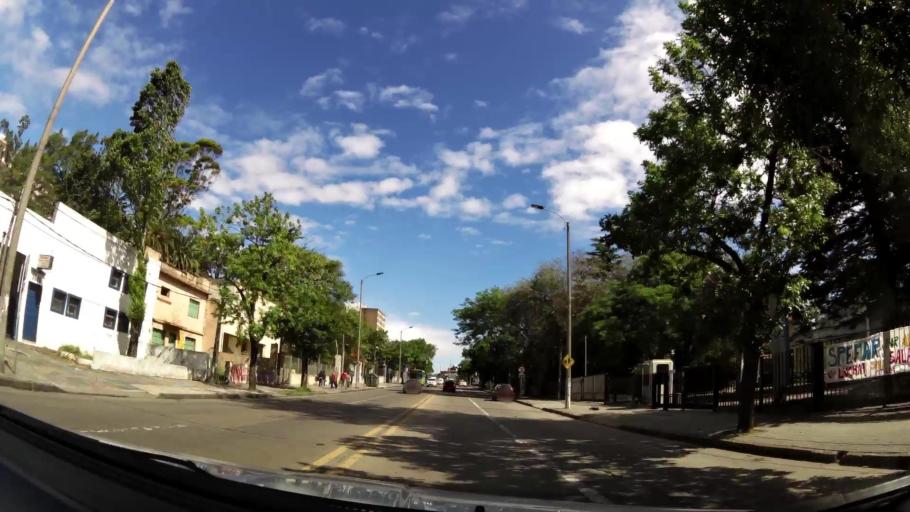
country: UY
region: Montevideo
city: Montevideo
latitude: -34.8555
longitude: -56.1967
